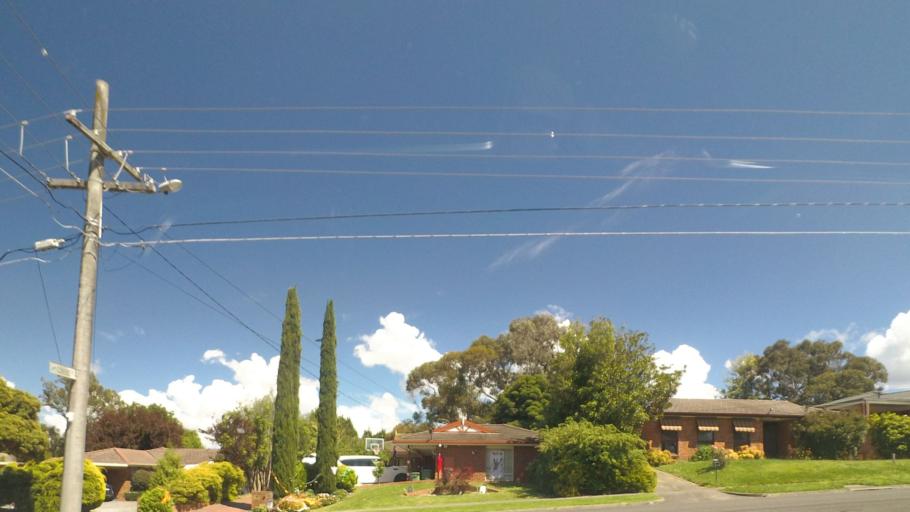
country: AU
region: Victoria
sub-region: Maroondah
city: Croydon South
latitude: -37.8182
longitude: 145.2777
